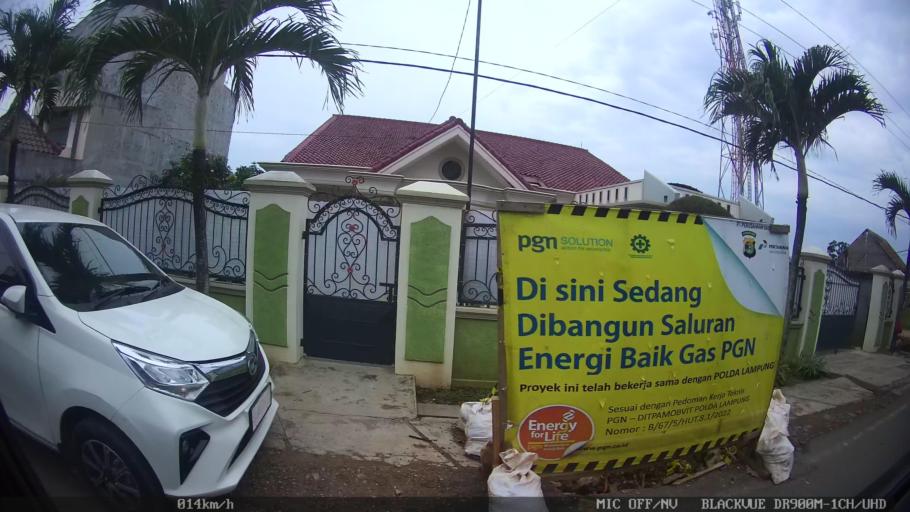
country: ID
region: Lampung
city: Kedaton
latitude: -5.3802
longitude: 105.2448
